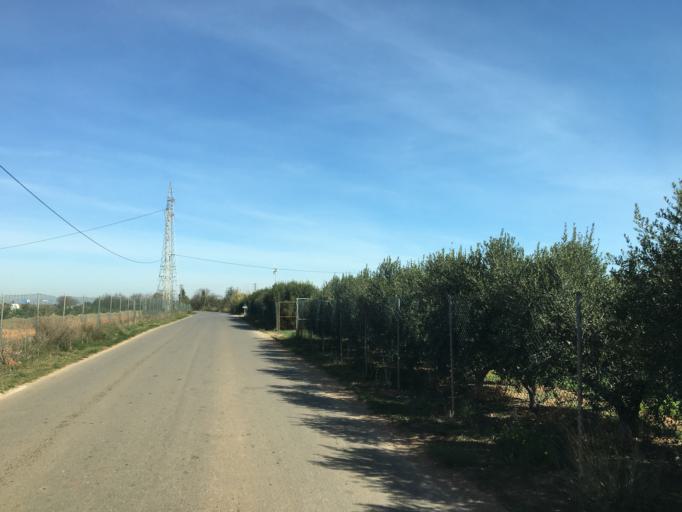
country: ES
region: Murcia
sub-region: Murcia
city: Cartagena
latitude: 37.6495
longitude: -1.0254
